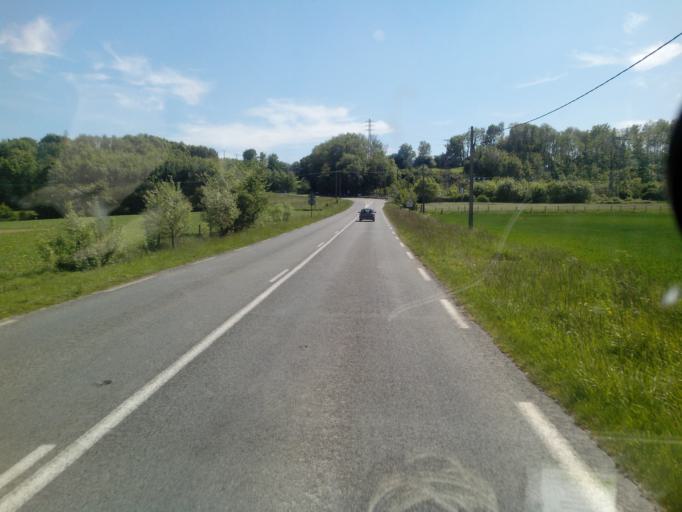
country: FR
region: Nord-Pas-de-Calais
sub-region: Departement du Pas-de-Calais
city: Samer
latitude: 50.6123
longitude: 1.7407
